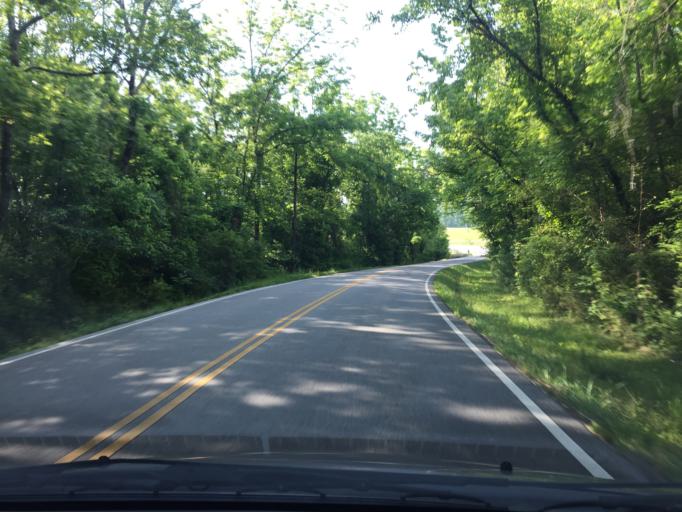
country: US
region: Tennessee
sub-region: Hamilton County
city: Apison
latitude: 35.0537
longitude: -85.0169
